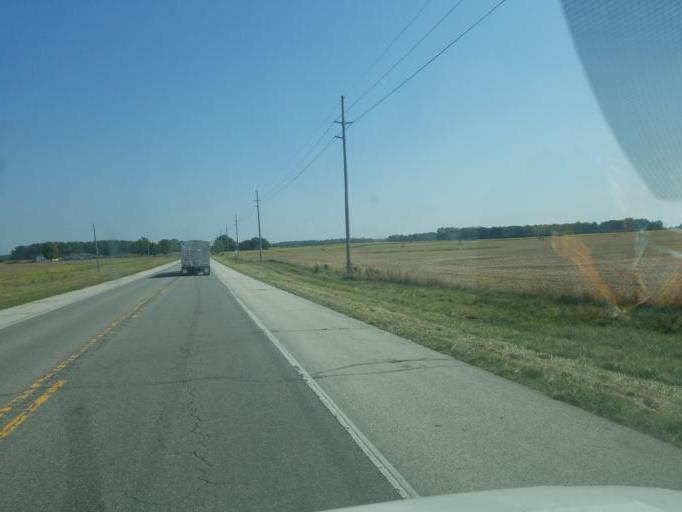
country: US
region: Indiana
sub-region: LaGrange County
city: Lagrange
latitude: 41.6419
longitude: -85.2409
